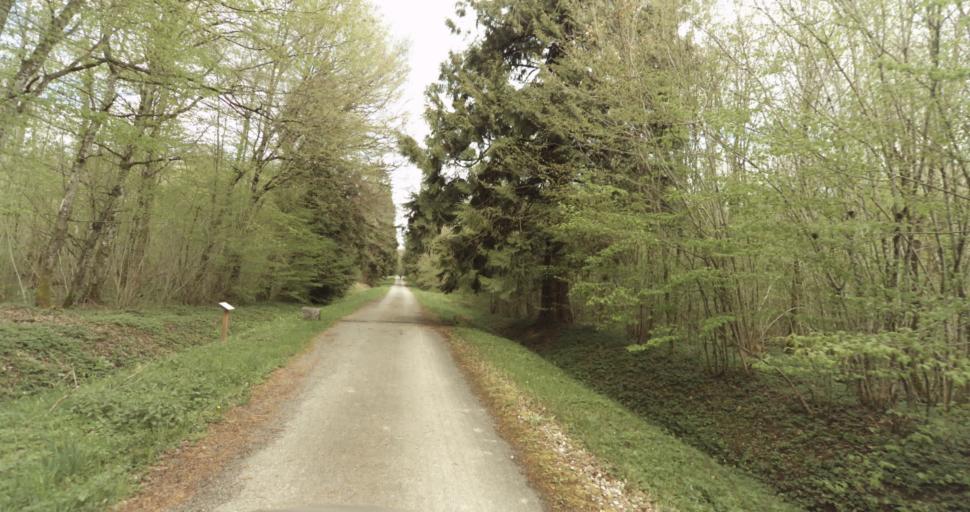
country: FR
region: Bourgogne
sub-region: Departement de la Cote-d'Or
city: Auxonne
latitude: 47.1656
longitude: 5.4234
